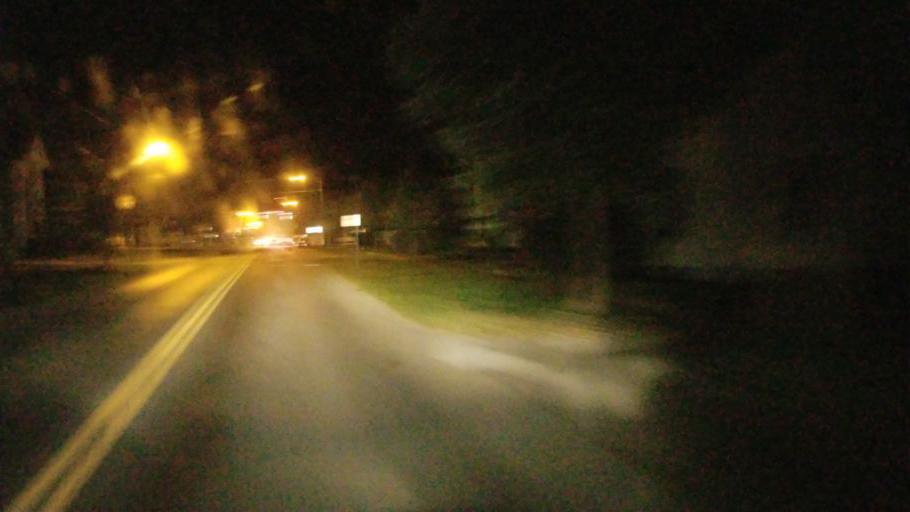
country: US
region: Ohio
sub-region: Hancock County
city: Arlington
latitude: 40.7872
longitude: -83.6430
